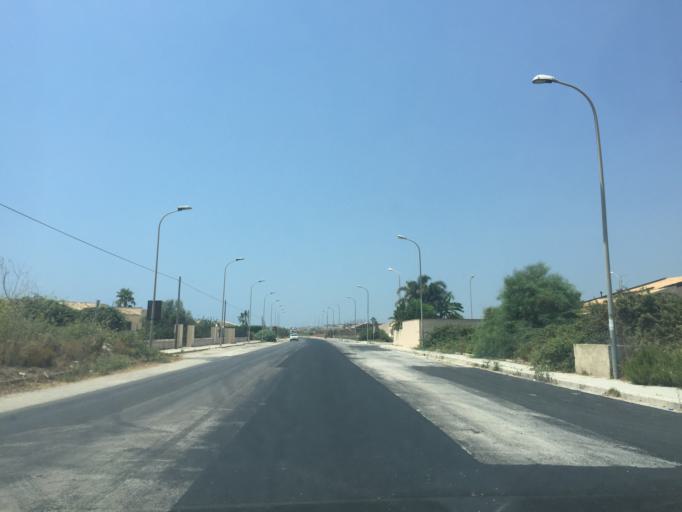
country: IT
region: Sicily
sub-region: Ragusa
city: Marina di Ragusa
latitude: 36.7796
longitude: 14.5824
